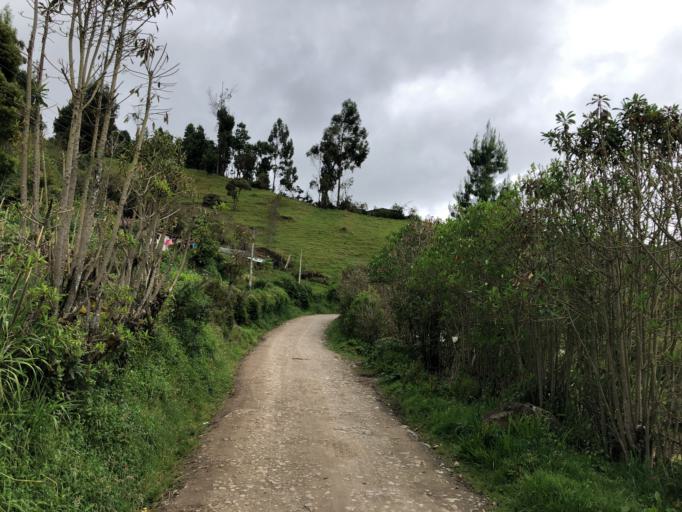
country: CO
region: Cauca
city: Totoro
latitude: 2.5065
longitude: -76.3600
